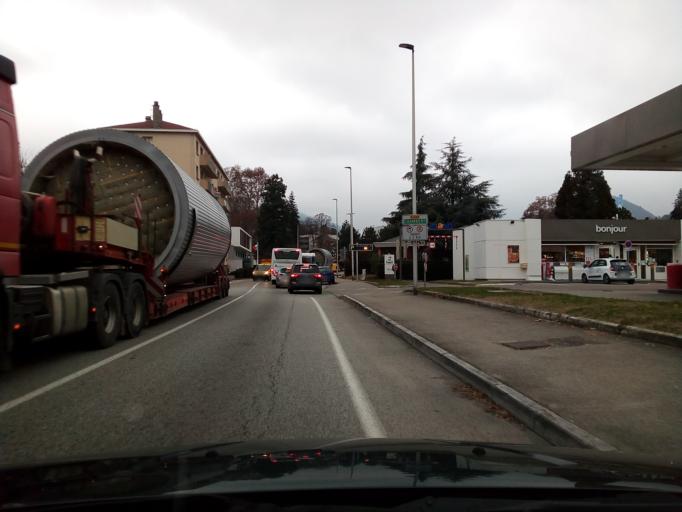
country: FR
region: Rhone-Alpes
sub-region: Departement de l'Isere
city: Voiron
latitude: 45.3586
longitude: 5.5920
